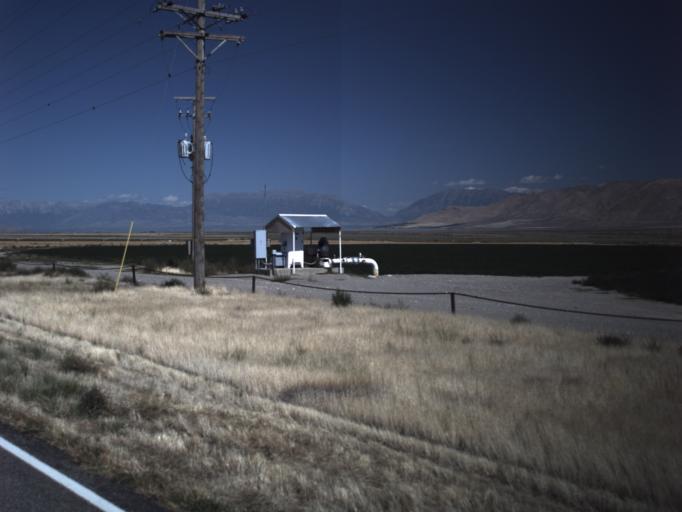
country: US
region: Utah
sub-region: Utah County
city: Genola
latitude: 40.0132
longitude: -111.9582
